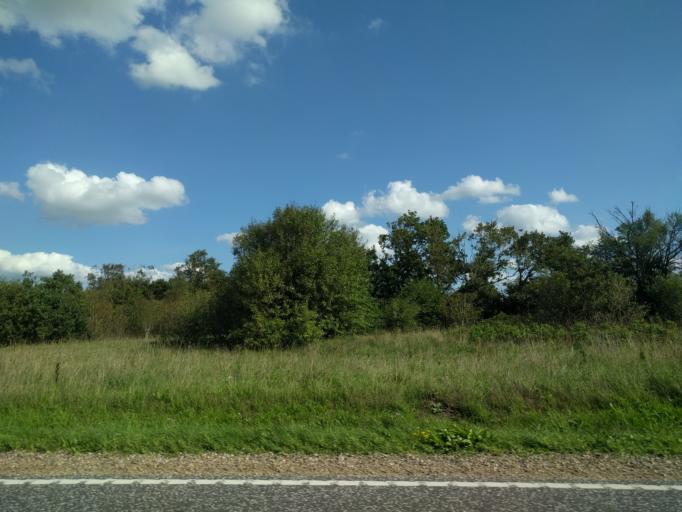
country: DK
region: Central Jutland
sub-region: Skive Kommune
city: Skive
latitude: 56.4752
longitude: 8.9583
